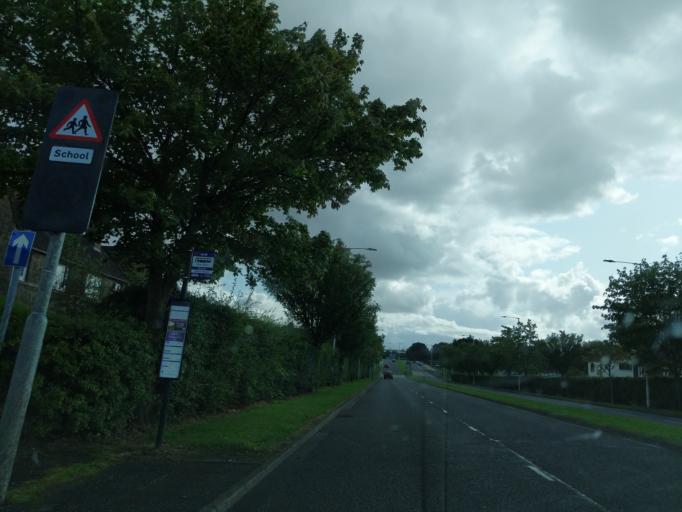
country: GB
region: Scotland
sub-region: Fife
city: Rosyth
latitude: 56.0396
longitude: -3.4277
